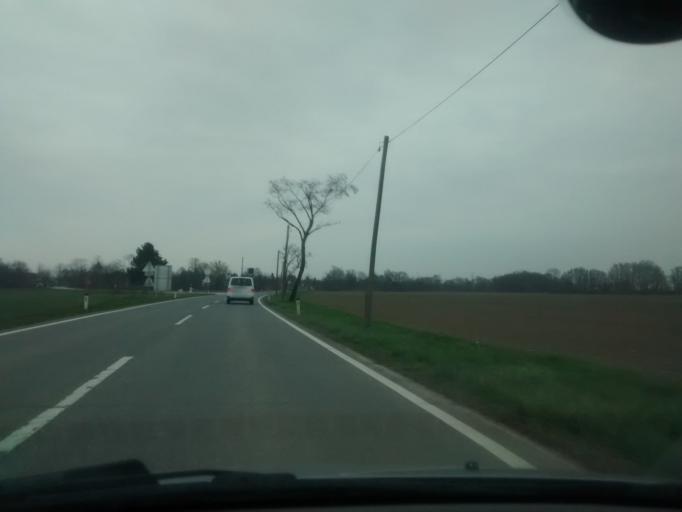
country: AT
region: Lower Austria
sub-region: Politischer Bezirk Modling
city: Achau
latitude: 48.0754
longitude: 16.3870
